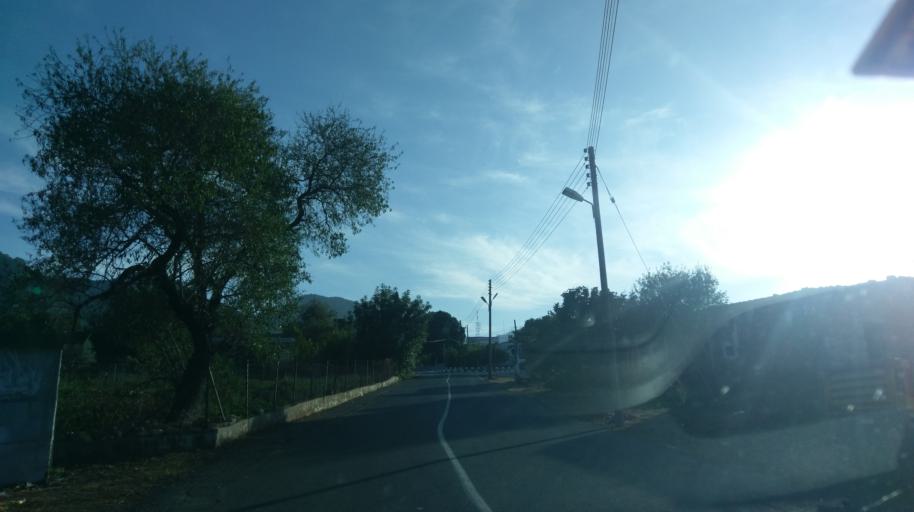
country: CY
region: Ammochostos
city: Lefkonoiko
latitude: 35.3377
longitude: 33.5846
